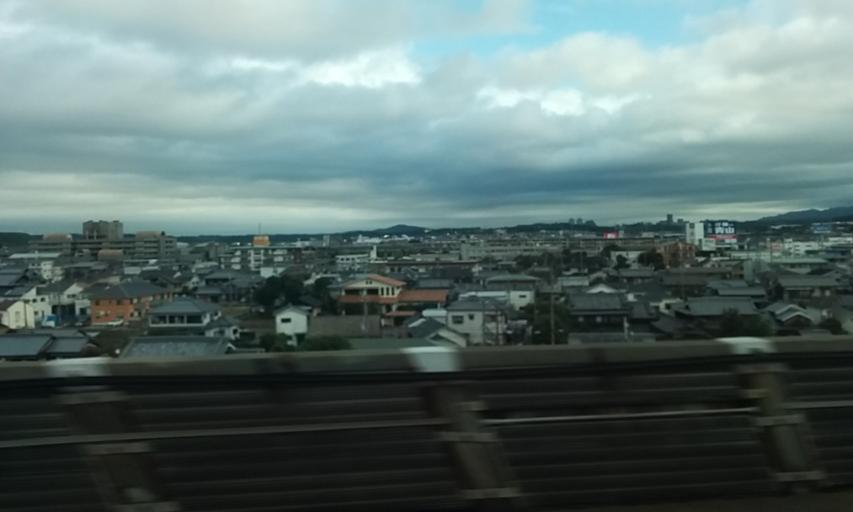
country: JP
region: Hyogo
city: Akashi
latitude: 34.6657
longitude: 134.9775
